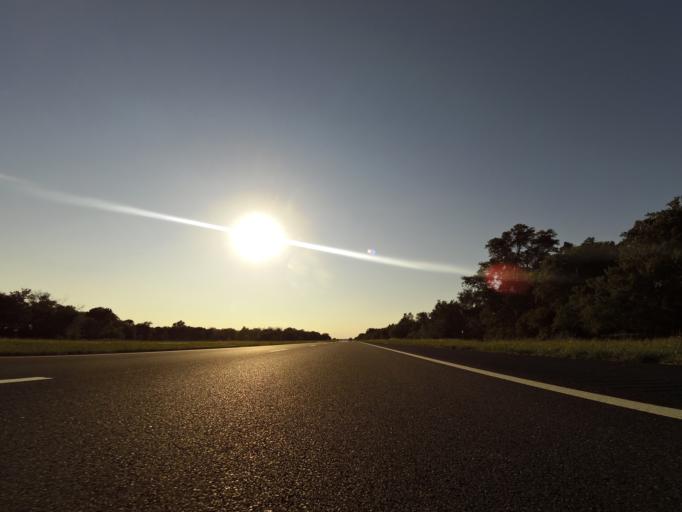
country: US
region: Kansas
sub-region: Reno County
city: Haven
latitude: 37.8842
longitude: -97.7279
